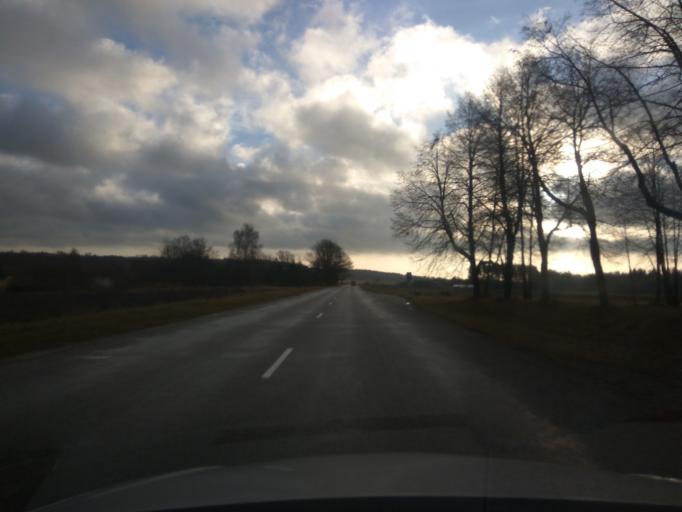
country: LV
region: Kuldigas Rajons
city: Kuldiga
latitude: 56.9331
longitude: 22.0371
